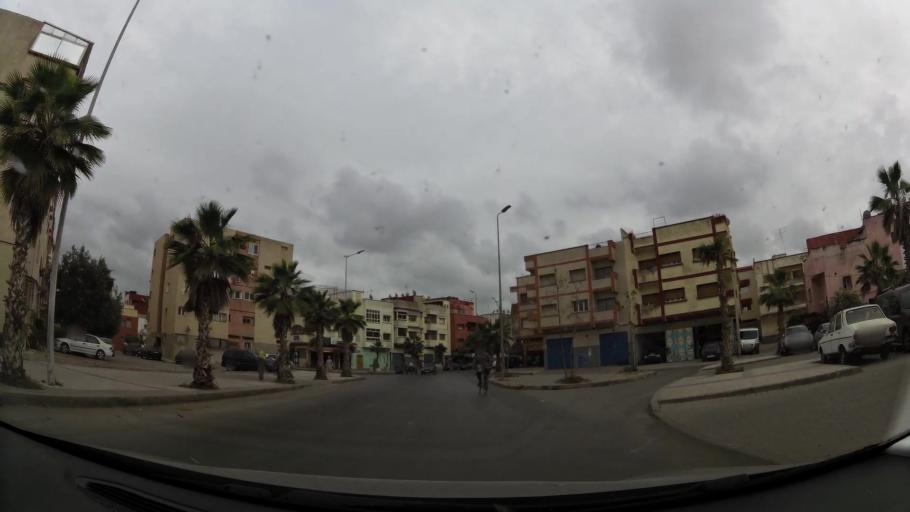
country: MA
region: Rabat-Sale-Zemmour-Zaer
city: Sale
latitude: 34.0493
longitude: -6.7979
